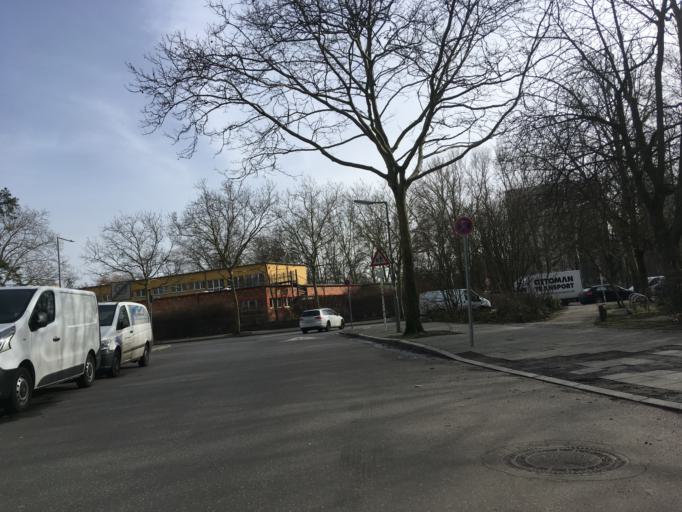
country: DE
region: Berlin
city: Markisches Viertel
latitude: 52.6010
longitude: 13.3621
